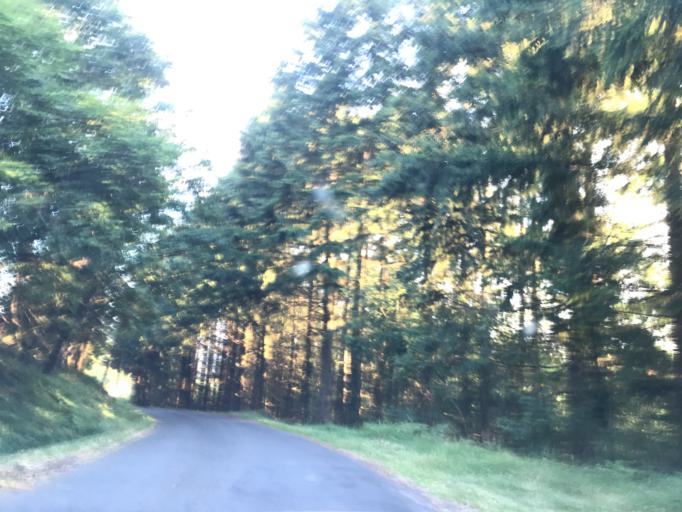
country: FR
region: Auvergne
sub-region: Departement du Puy-de-Dome
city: Courpiere
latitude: 45.7534
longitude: 3.6242
